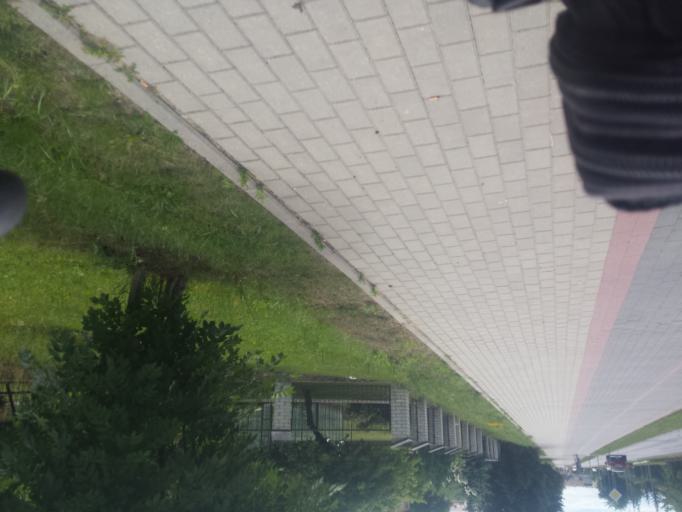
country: PL
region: Warmian-Masurian Voivodeship
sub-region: Powiat ilawski
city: Ilawa
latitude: 53.6100
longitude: 19.5699
